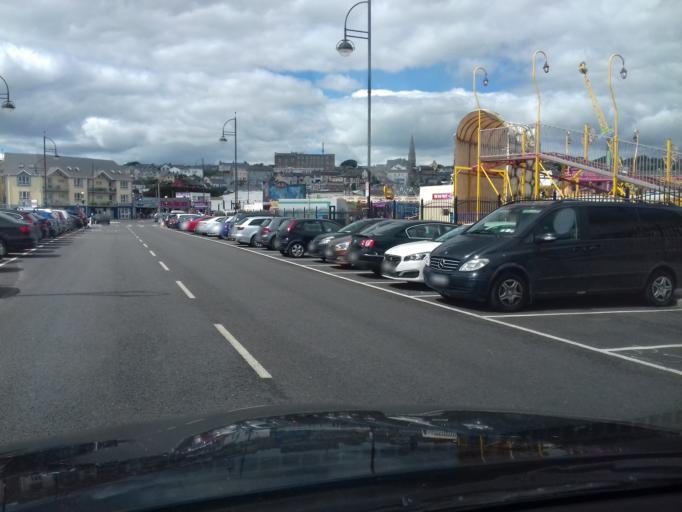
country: IE
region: Munster
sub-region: Waterford
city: Tra Mhor
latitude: 52.1595
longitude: -7.1457
